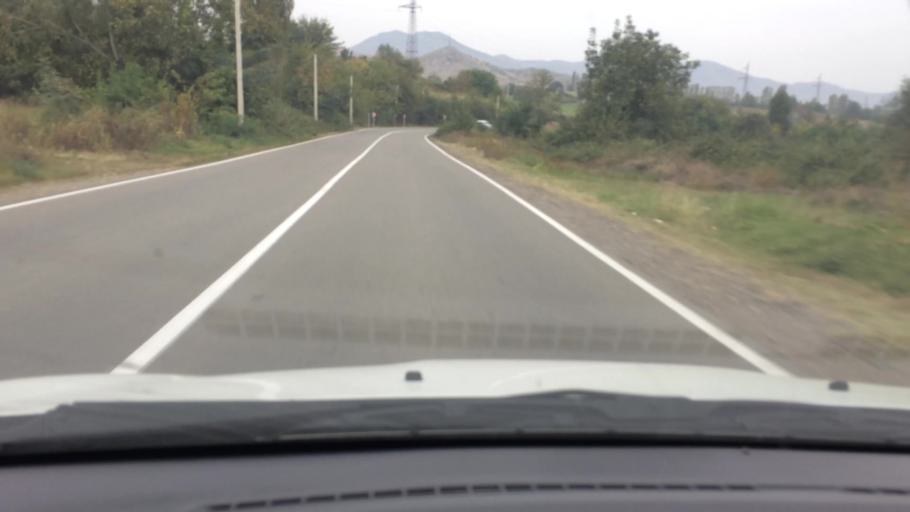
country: AM
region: Tavush
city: Bagratashen
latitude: 41.2651
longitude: 44.7934
